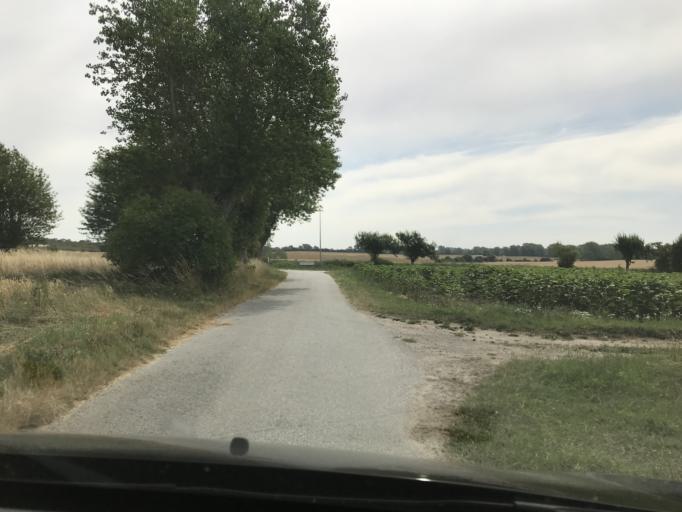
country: DK
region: South Denmark
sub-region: AEro Kommune
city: AEroskobing
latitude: 54.9102
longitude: 10.2774
